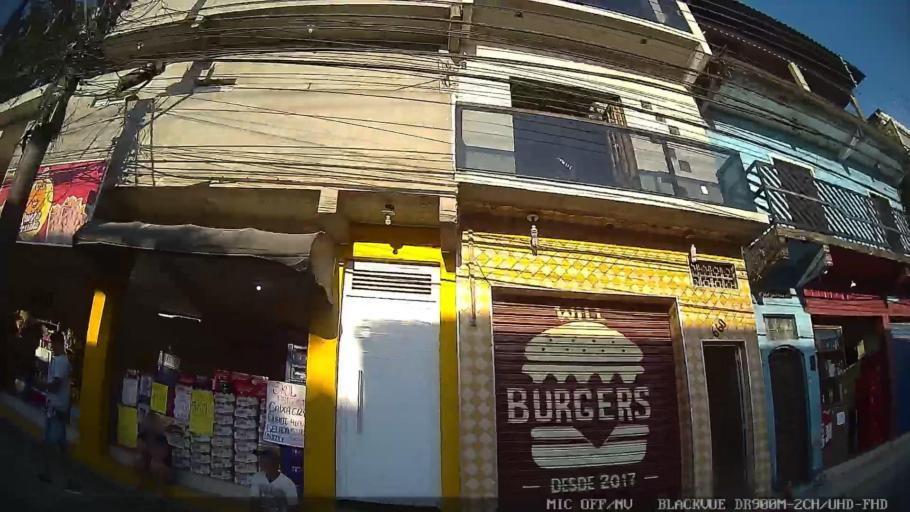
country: BR
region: Sao Paulo
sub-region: Guaruja
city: Guaruja
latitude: -23.9798
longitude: -46.2608
